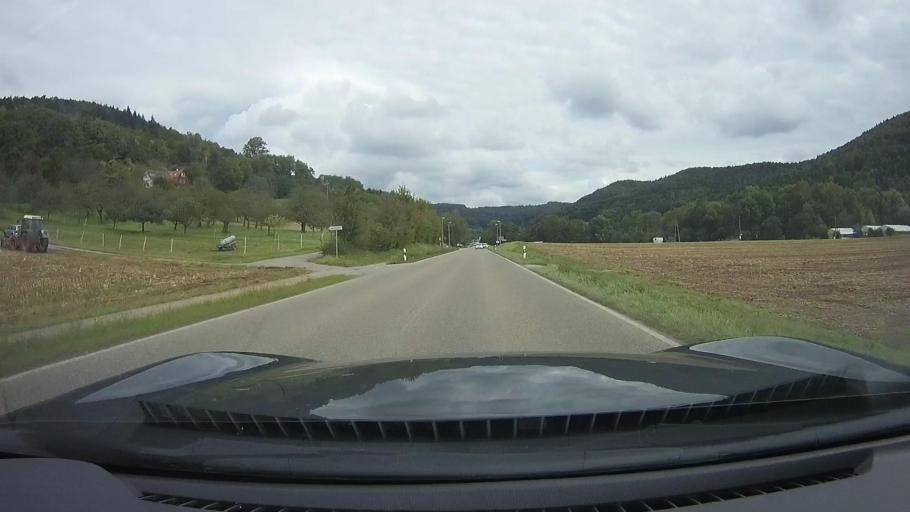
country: DE
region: Baden-Wuerttemberg
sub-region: Regierungsbezirk Stuttgart
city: Althutte
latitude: 48.8948
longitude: 9.5558
